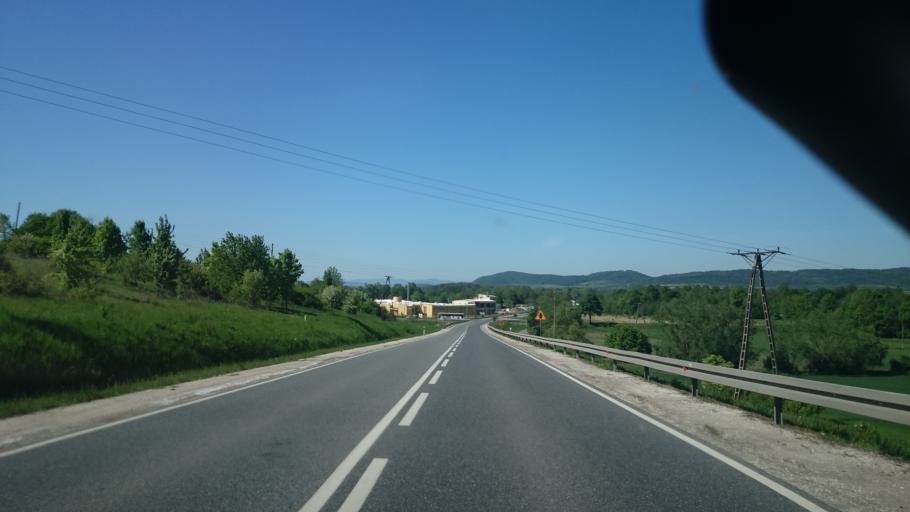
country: PL
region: Lower Silesian Voivodeship
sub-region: Powiat klodzki
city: Bystrzyca Klodzka
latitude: 50.3034
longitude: 16.6607
